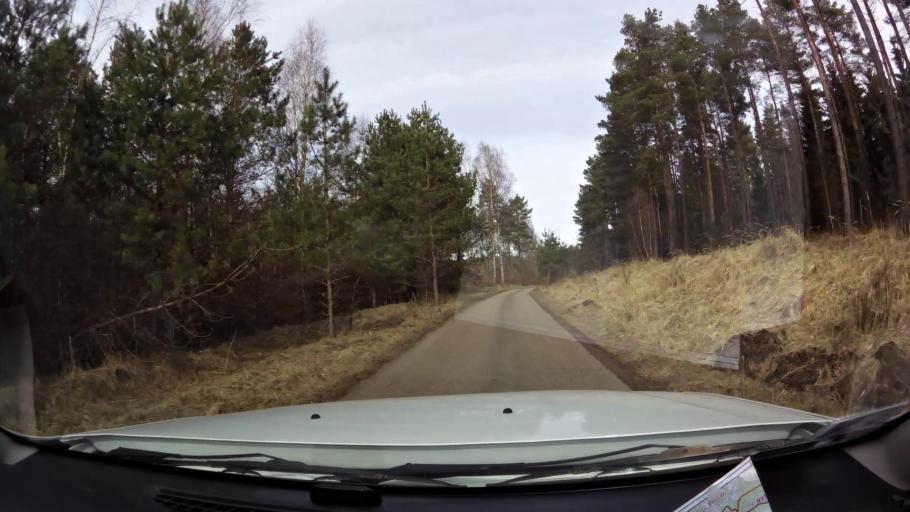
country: PL
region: West Pomeranian Voivodeship
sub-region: Powiat drawski
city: Drawsko Pomorskie
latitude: 53.4797
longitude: 15.6990
